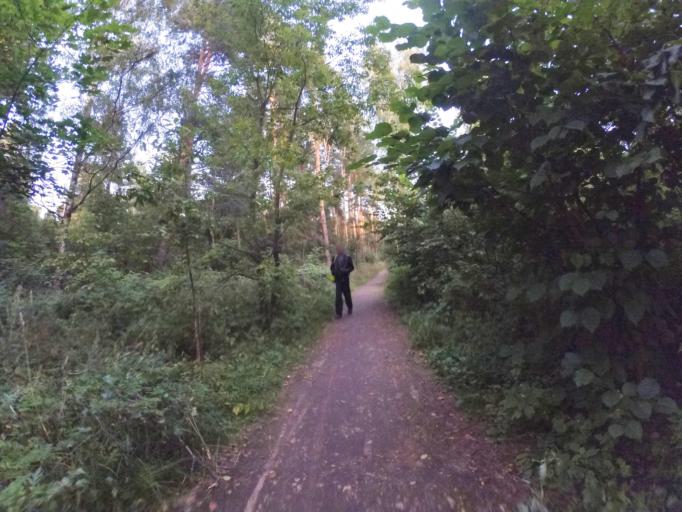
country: RU
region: Moscow
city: Vykhino-Zhulebino
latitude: 55.6872
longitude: 37.8153
